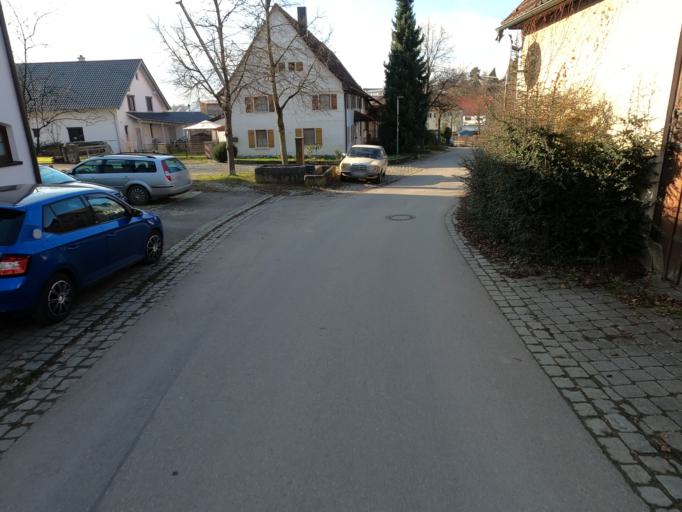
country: DE
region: Baden-Wuerttemberg
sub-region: Regierungsbezirk Stuttgart
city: Hattenhofen
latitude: 48.6681
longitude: 9.5793
